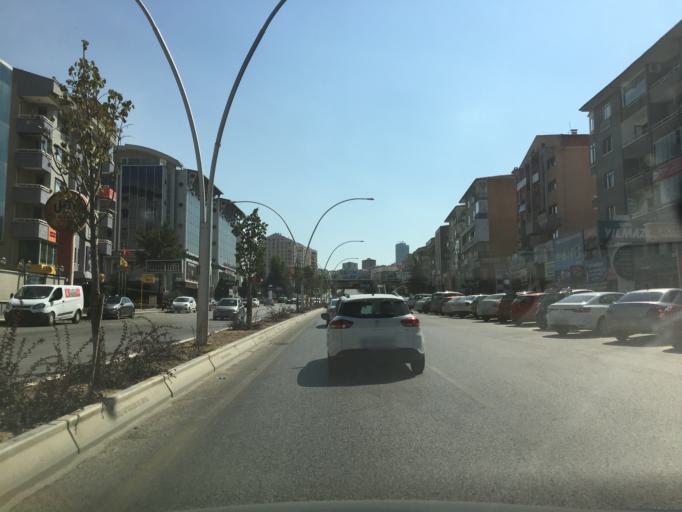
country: TR
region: Ankara
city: Cankaya
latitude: 39.8749
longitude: 32.8630
